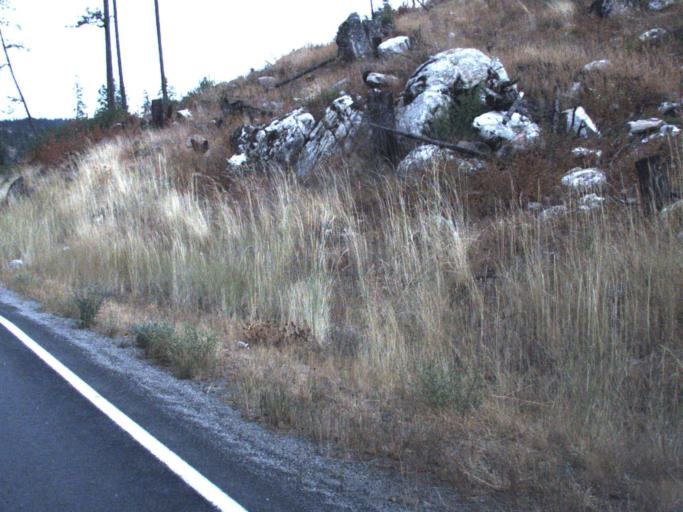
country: US
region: Washington
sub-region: Spokane County
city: Deer Park
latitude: 47.9745
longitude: -117.7344
